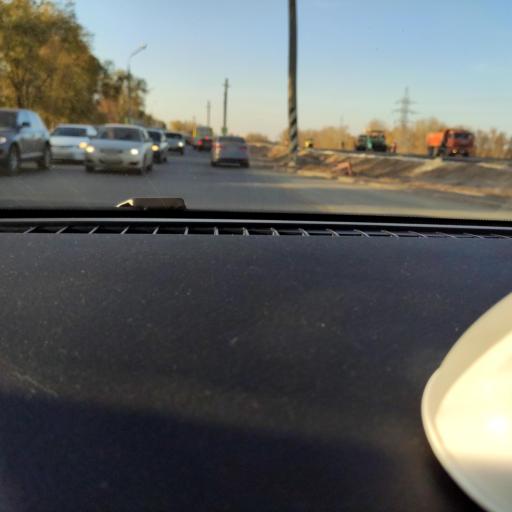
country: RU
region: Samara
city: Samara
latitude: 53.1400
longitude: 50.1011
